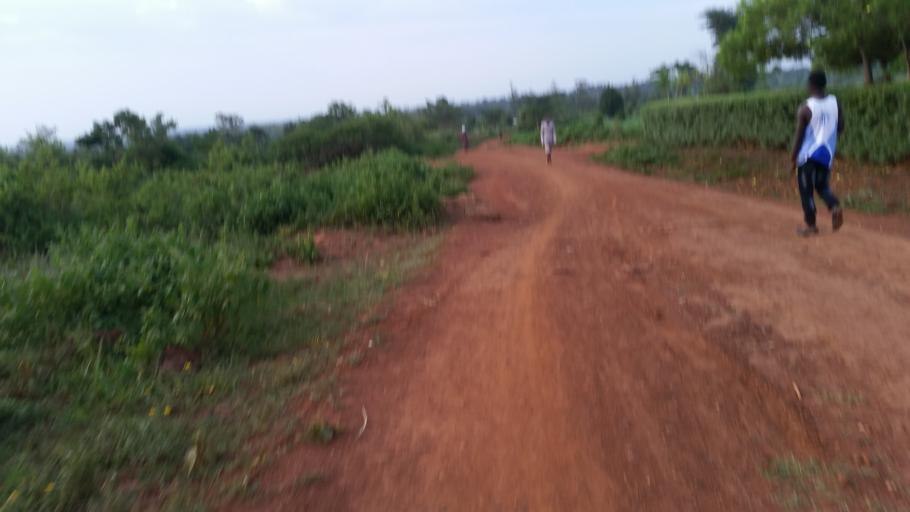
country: UG
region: Eastern Region
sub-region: Busia District
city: Busia
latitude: 0.5384
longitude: 34.0427
